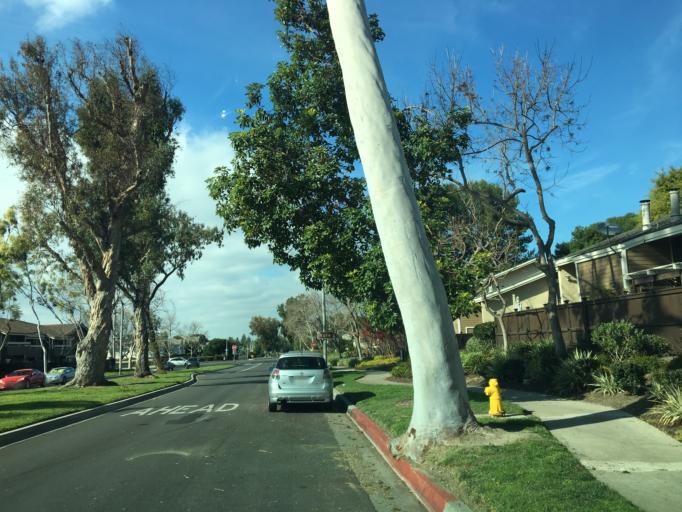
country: US
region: California
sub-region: Orange County
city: North Tustin
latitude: 33.7148
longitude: -117.7589
